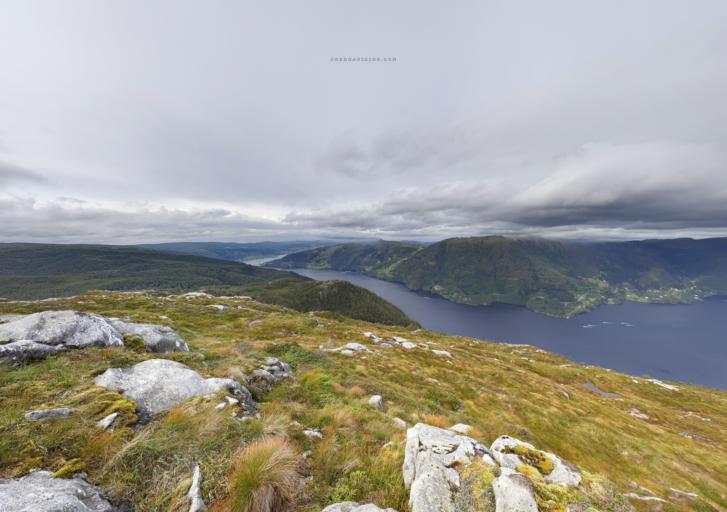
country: NO
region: Hordaland
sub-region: Bergen
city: Indre Arna
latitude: 60.4220
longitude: 5.6141
